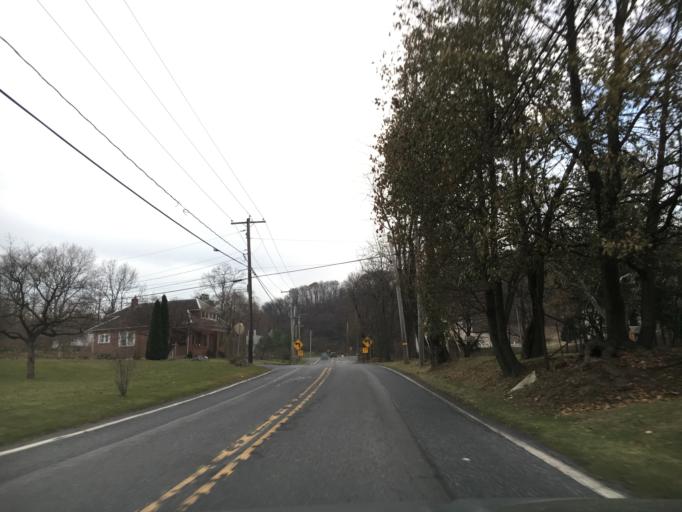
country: US
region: Pennsylvania
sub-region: Lehigh County
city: Slatington
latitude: 40.7232
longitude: -75.6146
